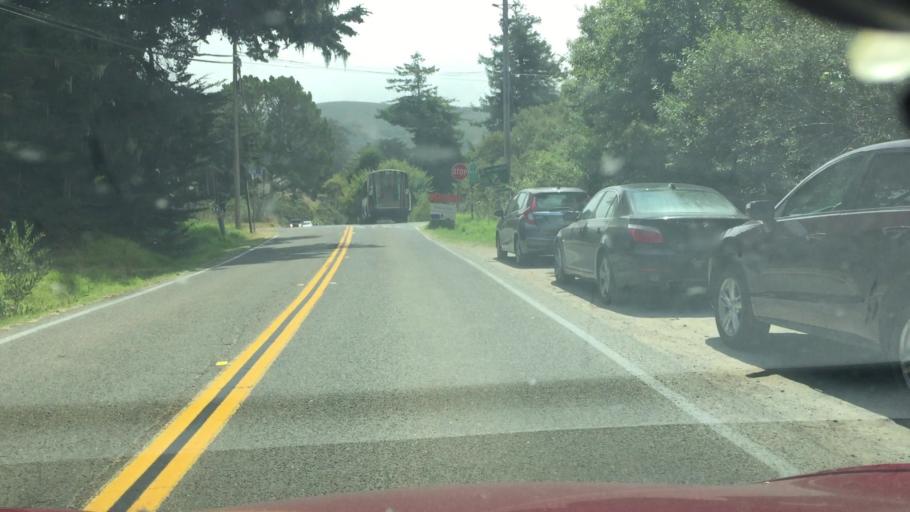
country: US
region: California
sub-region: Marin County
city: Tamalpais Valley
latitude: 37.8674
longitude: -122.5778
